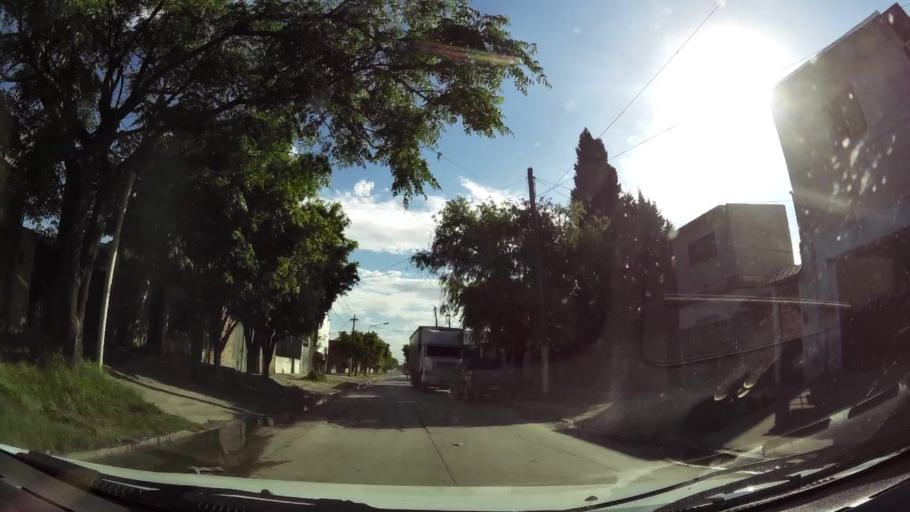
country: AR
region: Buenos Aires
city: Hurlingham
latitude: -34.5600
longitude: -58.6213
